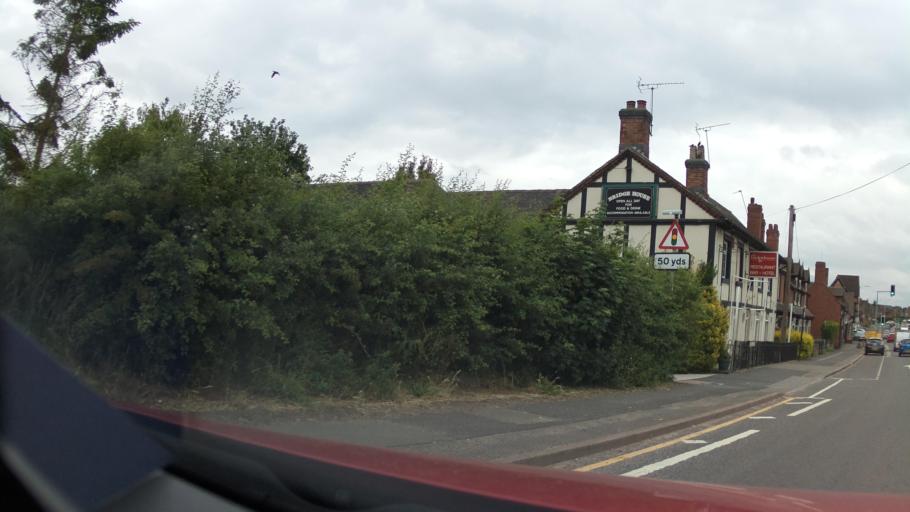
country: GB
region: England
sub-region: Staffordshire
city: Penkridge
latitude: 52.7271
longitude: -2.1165
